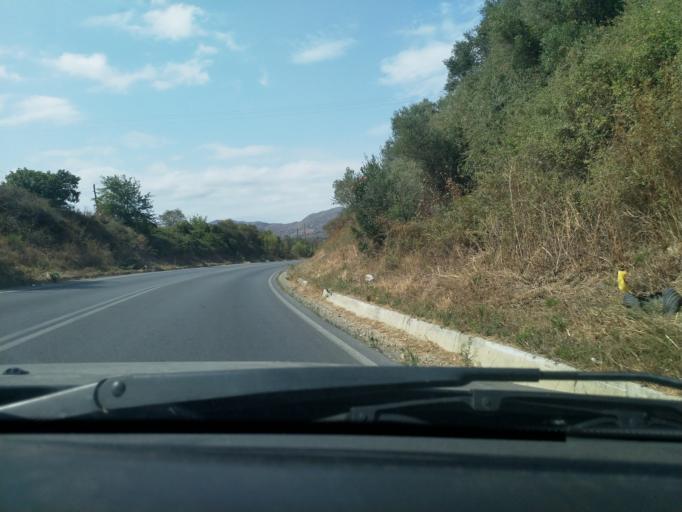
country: GR
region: Crete
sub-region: Nomos Rethymnis
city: Atsipopoulon
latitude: 35.2273
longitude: 24.4766
